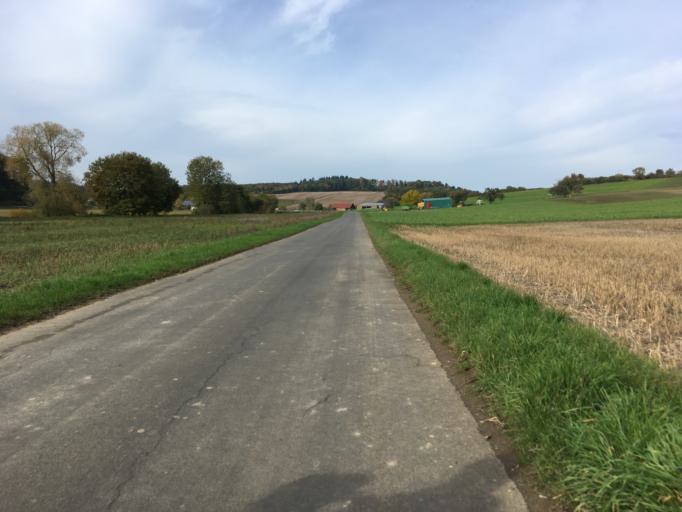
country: DE
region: Baden-Wuerttemberg
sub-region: Karlsruhe Region
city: Rosenberg
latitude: 49.4831
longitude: 9.4651
